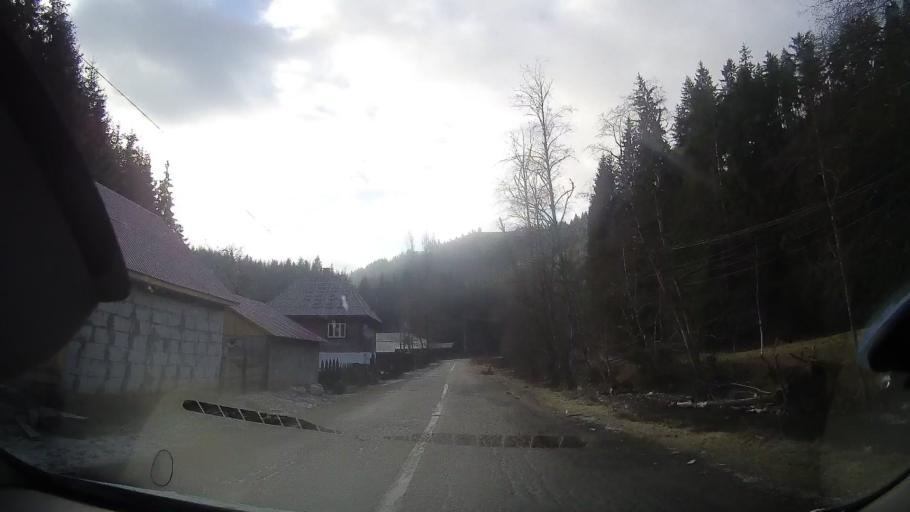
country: RO
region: Alba
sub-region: Comuna Albac
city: Albac
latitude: 46.4686
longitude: 22.9684
